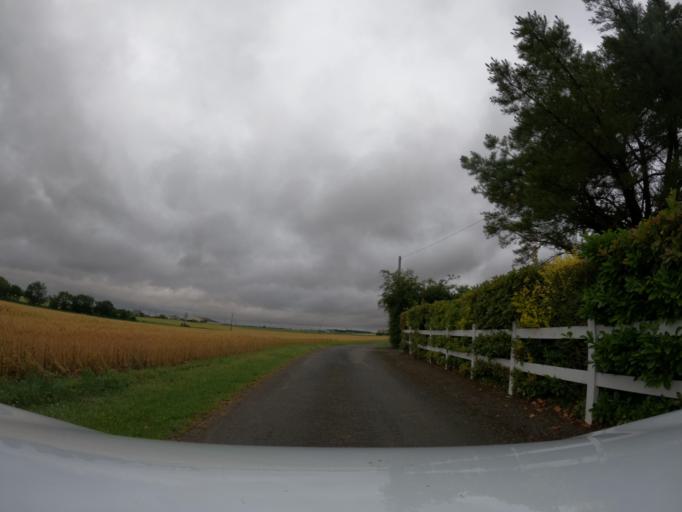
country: FR
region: Pays de la Loire
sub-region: Departement de la Vendee
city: Maillezais
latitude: 46.4029
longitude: -0.7388
